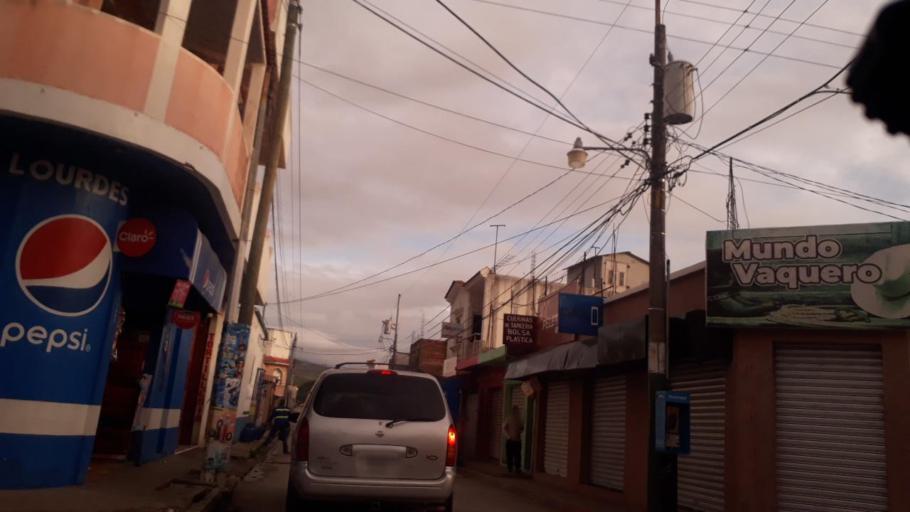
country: GT
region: Jutiapa
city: El Progreso
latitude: 14.3580
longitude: -89.8477
